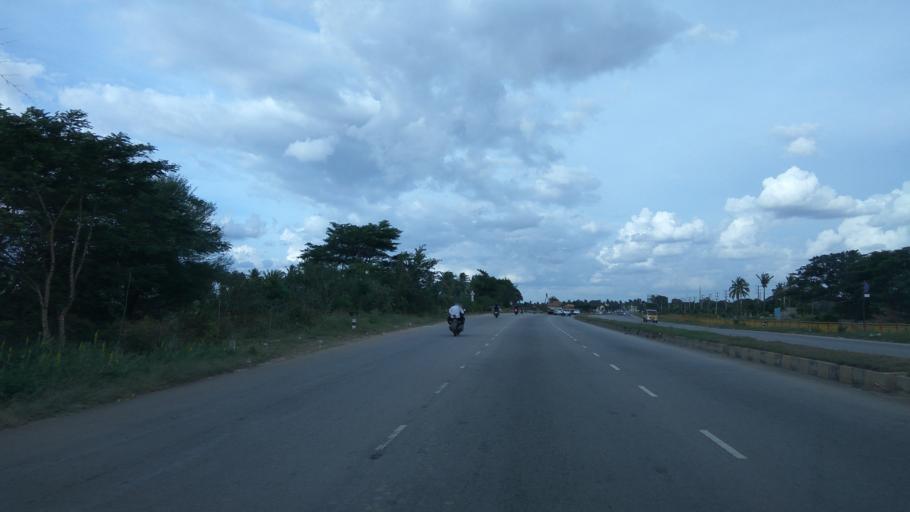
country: IN
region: Karnataka
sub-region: Bangalore Rural
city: Devanhalli
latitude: 13.2370
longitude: 77.6973
